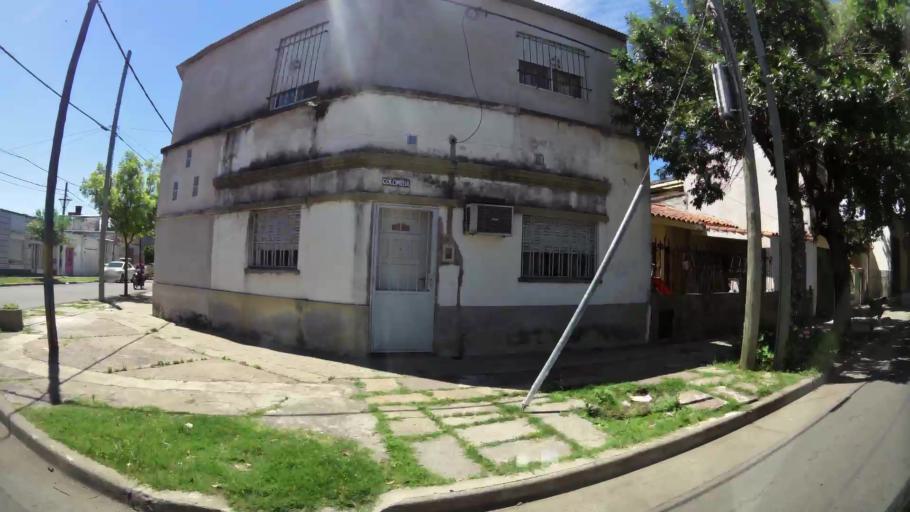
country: AR
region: Santa Fe
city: Perez
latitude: -32.9448
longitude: -60.7159
